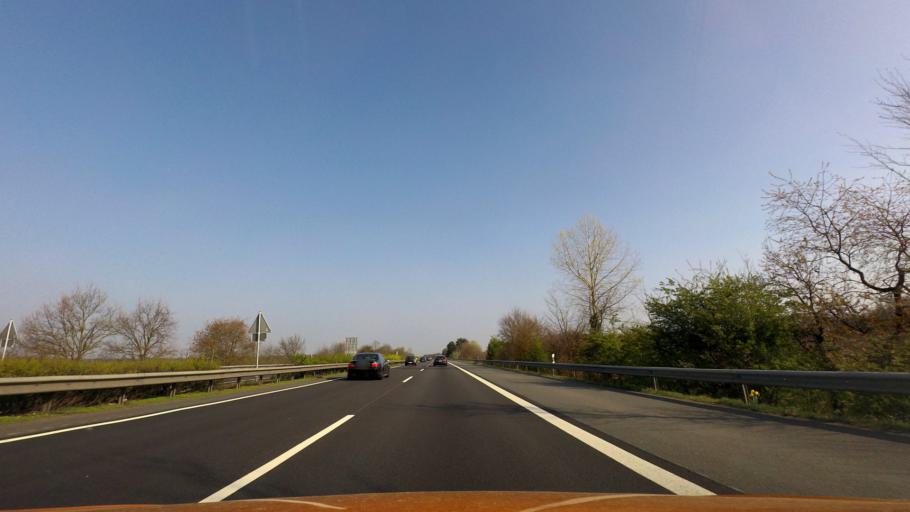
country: DE
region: Lower Saxony
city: Holdorf
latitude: 52.5555
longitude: 8.1138
